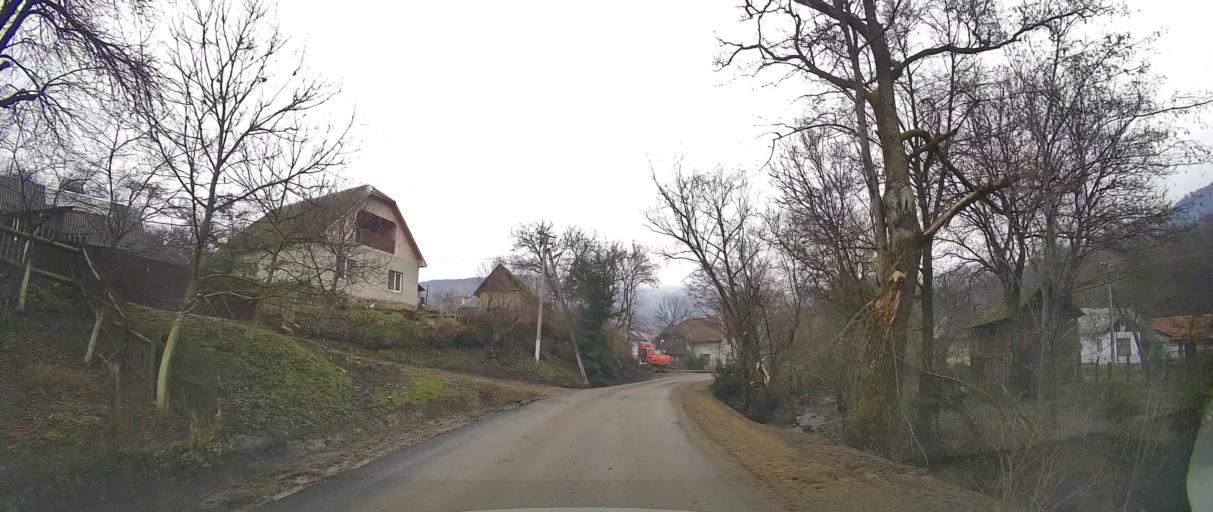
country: UA
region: Zakarpattia
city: Velykyi Bereznyi
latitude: 48.9672
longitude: 22.5511
